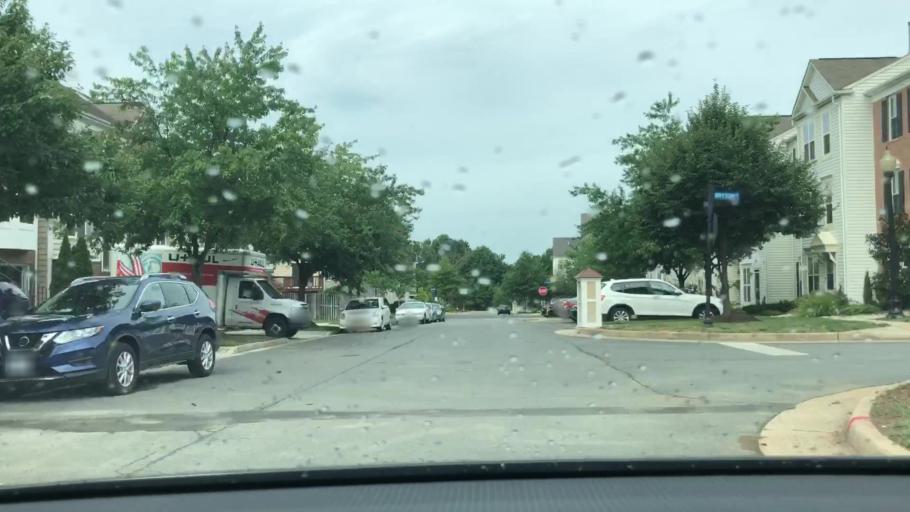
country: US
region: Virginia
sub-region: Loudoun County
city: South Riding
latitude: 38.9147
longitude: -77.5152
